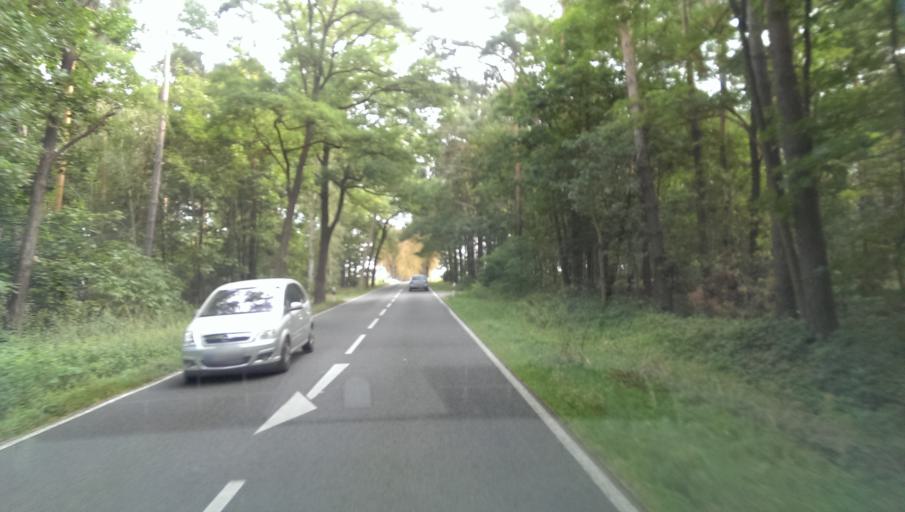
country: DE
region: Brandenburg
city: Am Mellensee
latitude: 52.2286
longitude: 13.3394
